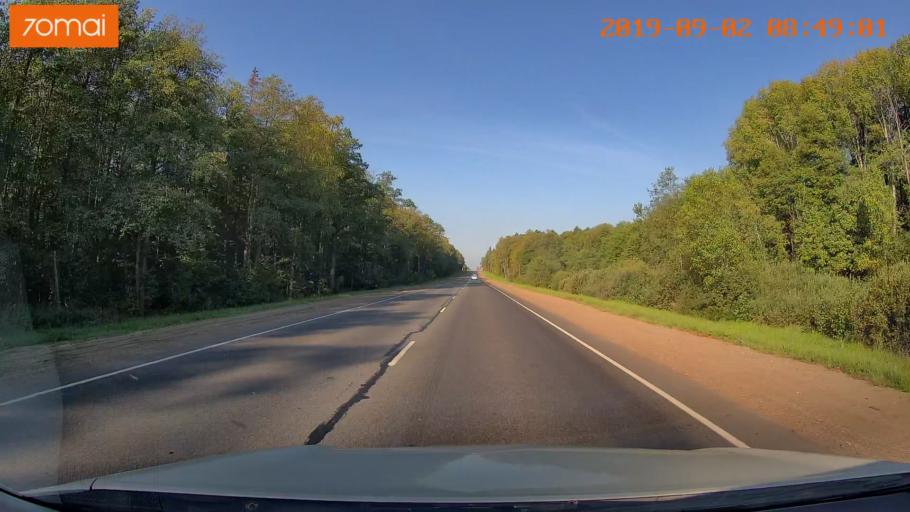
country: RU
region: Kaluga
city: Medyn'
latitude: 54.9665
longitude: 35.9173
